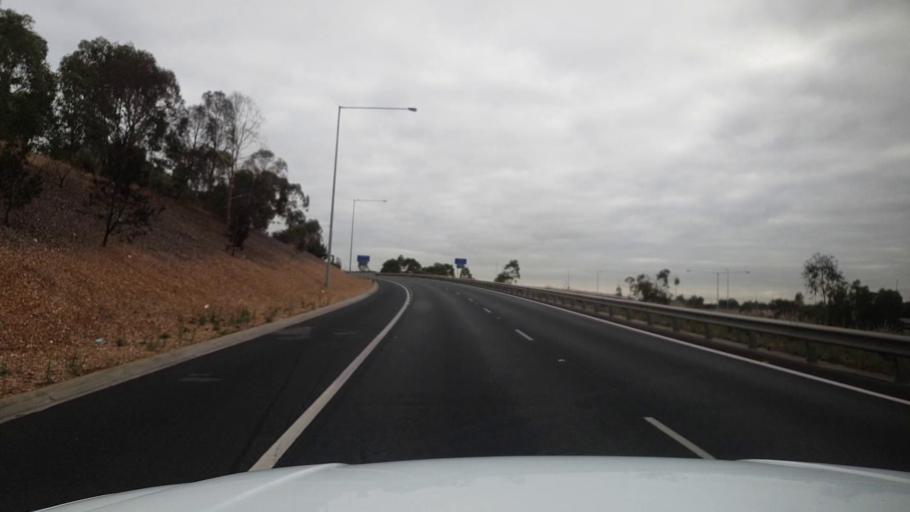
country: AU
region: Victoria
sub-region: Greater Dandenong
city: Noble Park North
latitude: -37.9485
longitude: 145.2040
